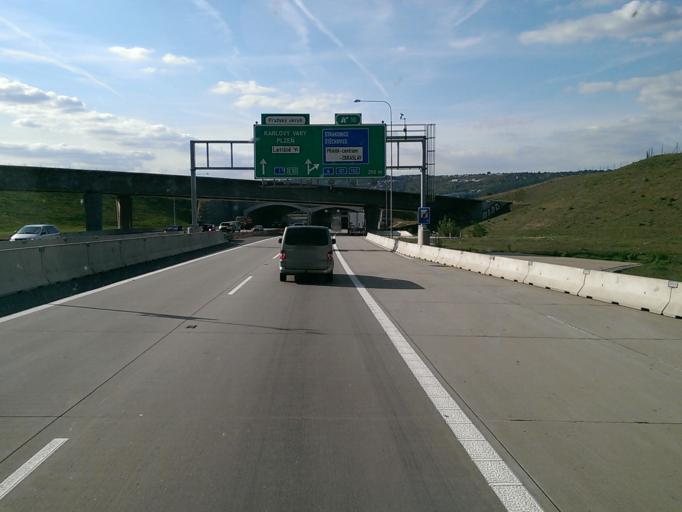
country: CZ
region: Central Bohemia
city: Dolni Brezany
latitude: 49.9823
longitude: 14.4316
